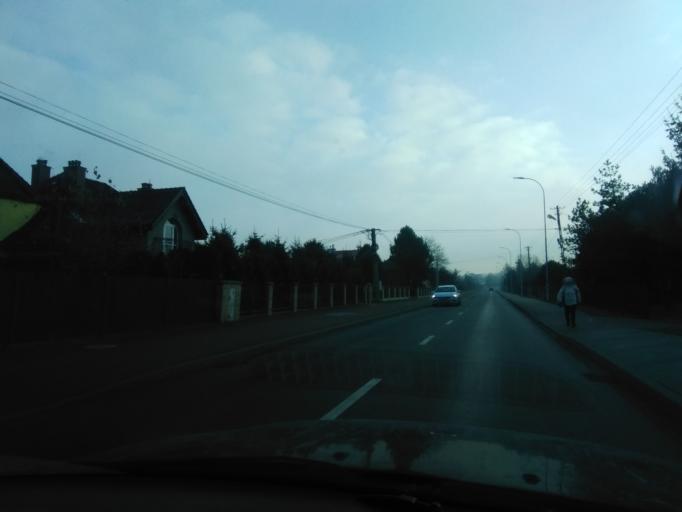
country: PL
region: Subcarpathian Voivodeship
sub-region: Powiat rzeszowski
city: Tyczyn
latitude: 49.9770
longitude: 21.9930
